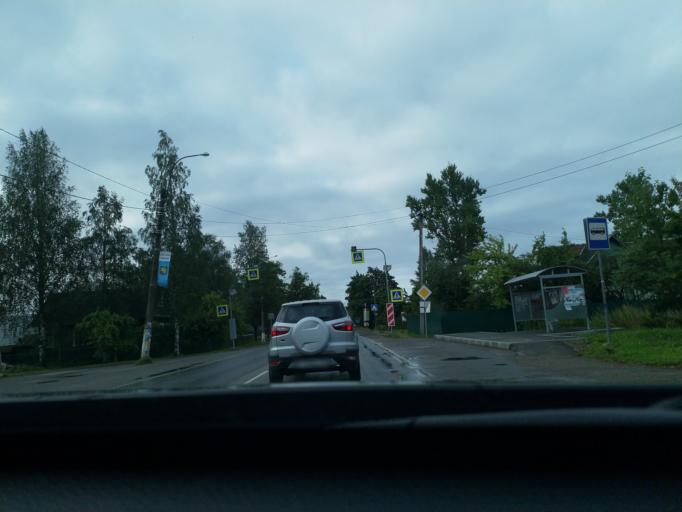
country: RU
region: Leningrad
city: Nikol'skoye
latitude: 59.6930
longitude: 30.7850
